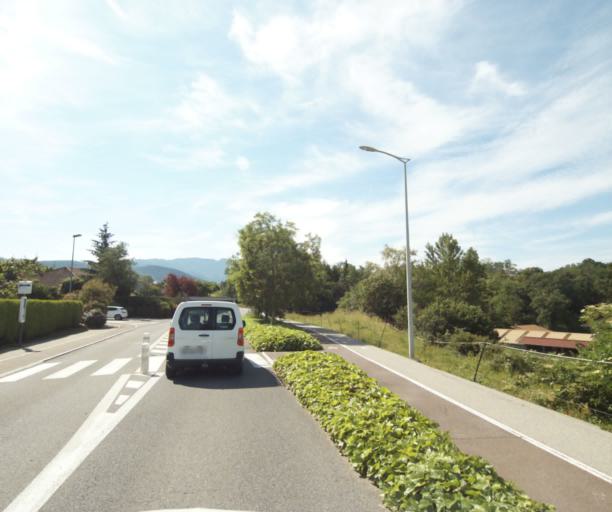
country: FR
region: Rhone-Alpes
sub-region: Departement de la Haute-Savoie
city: Margencel
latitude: 46.3405
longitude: 6.4154
